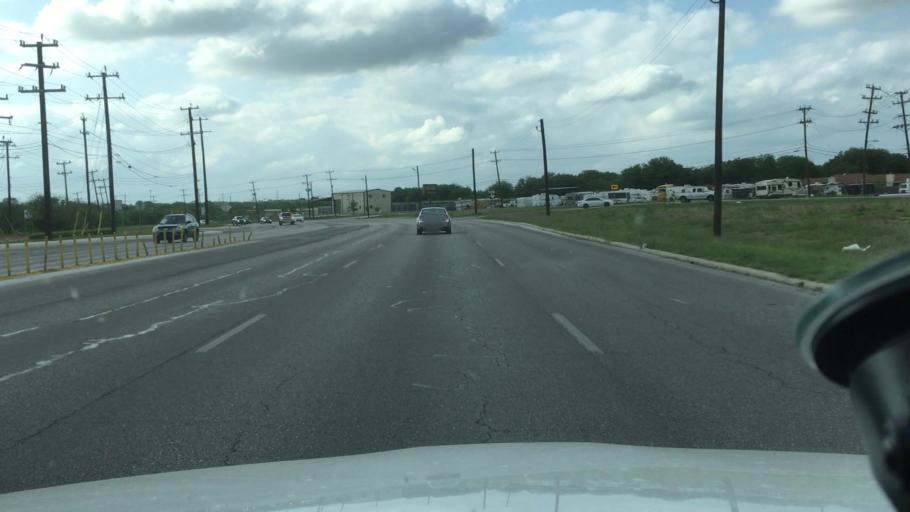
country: US
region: Texas
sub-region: Bexar County
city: Windcrest
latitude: 29.4984
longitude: -98.3500
